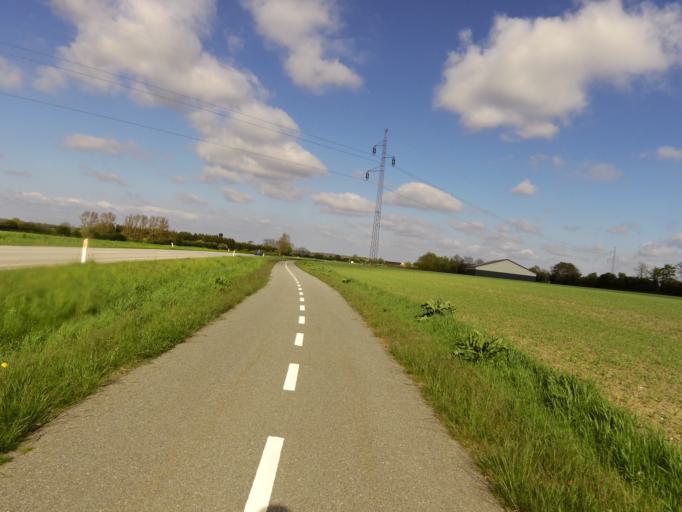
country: DK
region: South Denmark
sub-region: Vejen Kommune
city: Rodding
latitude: 55.3584
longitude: 9.0020
